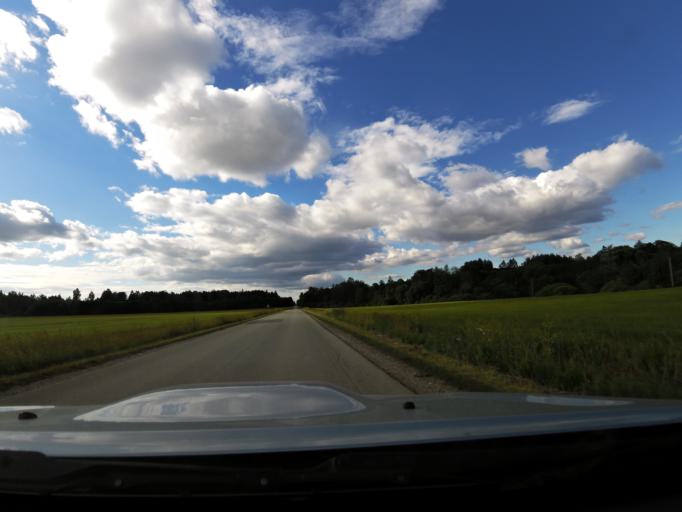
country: LT
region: Panevezys
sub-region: Birzai
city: Birzai
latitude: 56.3435
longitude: 24.7976
